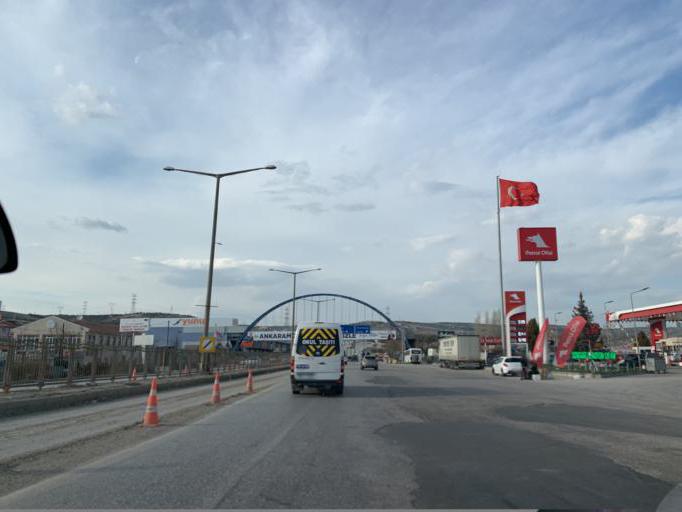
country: TR
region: Ankara
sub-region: Goelbasi
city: Golbasi
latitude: 39.7990
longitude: 32.8058
